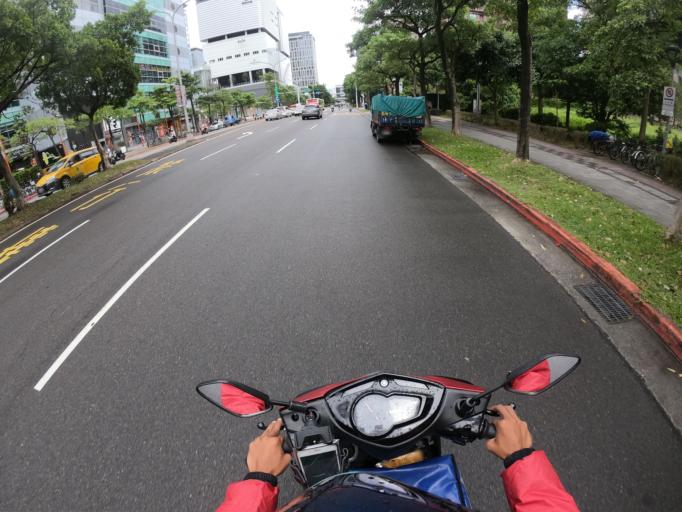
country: TW
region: Taipei
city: Taipei
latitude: 25.0349
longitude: 121.5685
